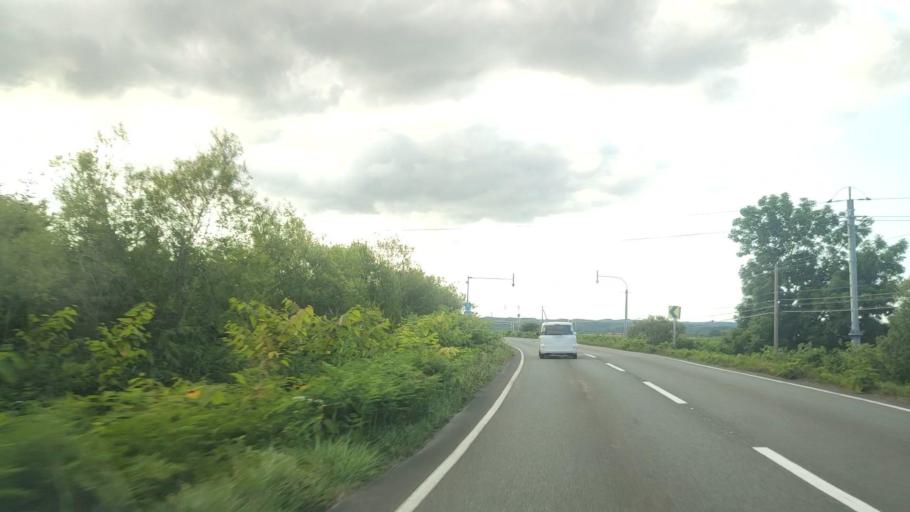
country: JP
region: Hokkaido
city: Makubetsu
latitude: 45.0035
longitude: 141.8142
